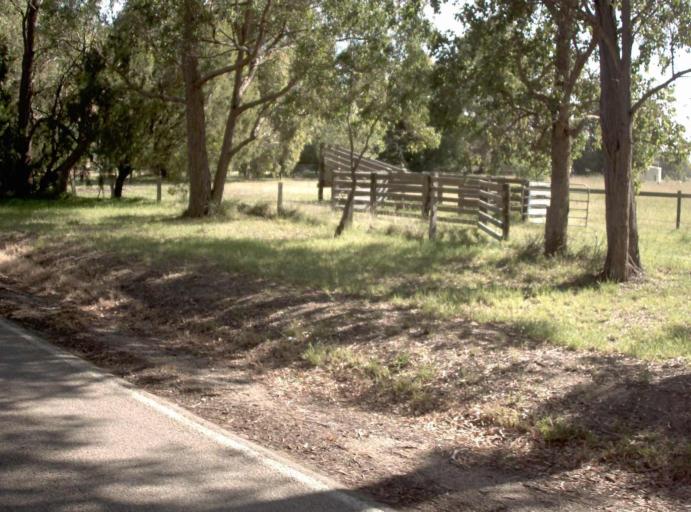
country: AU
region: Victoria
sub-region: East Gippsland
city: Lakes Entrance
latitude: -37.7700
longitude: 147.8130
